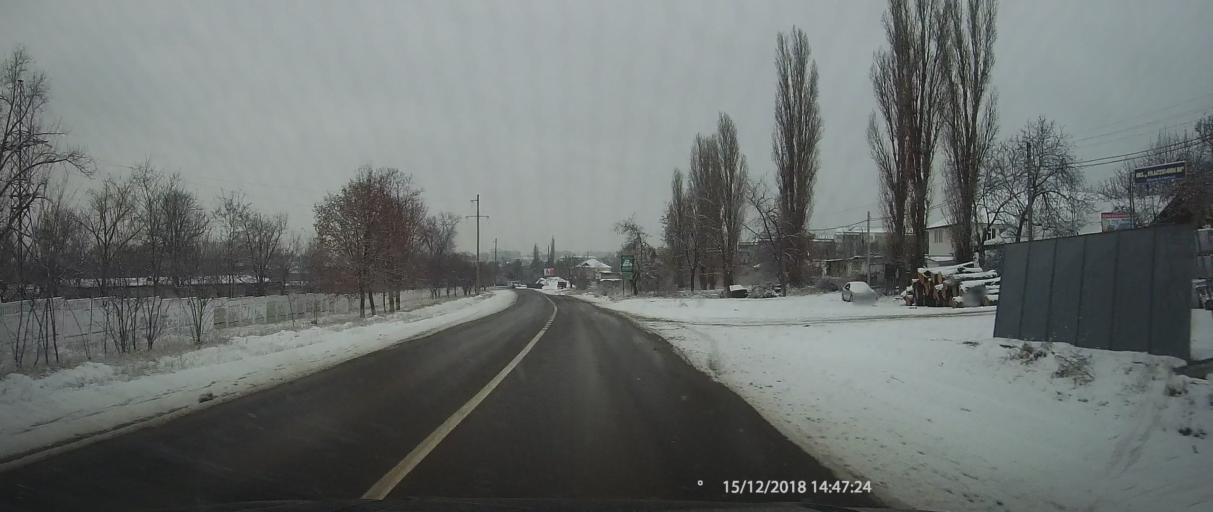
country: MD
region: Cahul
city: Cahul
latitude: 45.8933
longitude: 28.2066
